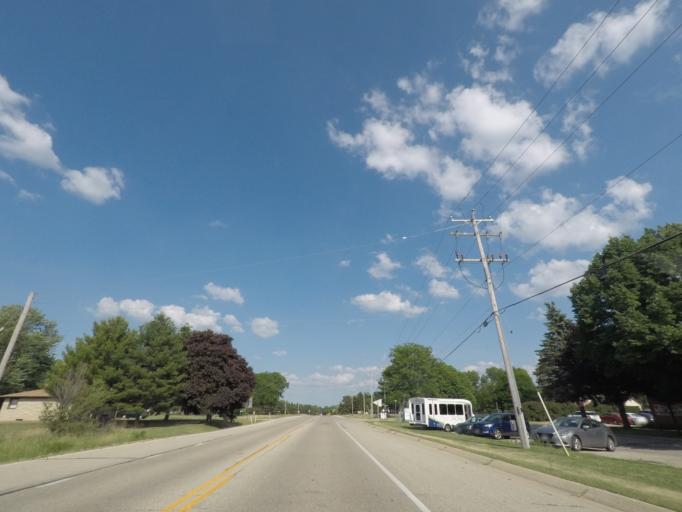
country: US
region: Wisconsin
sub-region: Walworth County
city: East Troy
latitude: 42.7922
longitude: -88.4238
